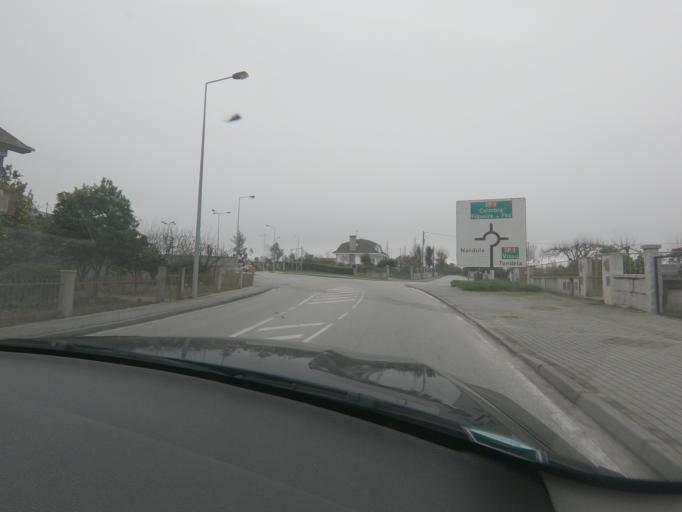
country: PT
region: Viseu
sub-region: Concelho de Tondela
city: Tondela
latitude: 40.5278
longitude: -8.0899
